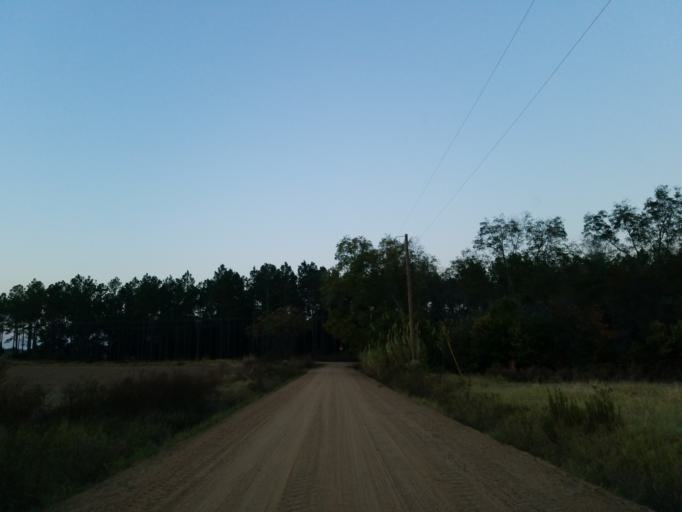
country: US
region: Georgia
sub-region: Turner County
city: Ashburn
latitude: 31.7457
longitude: -83.4861
